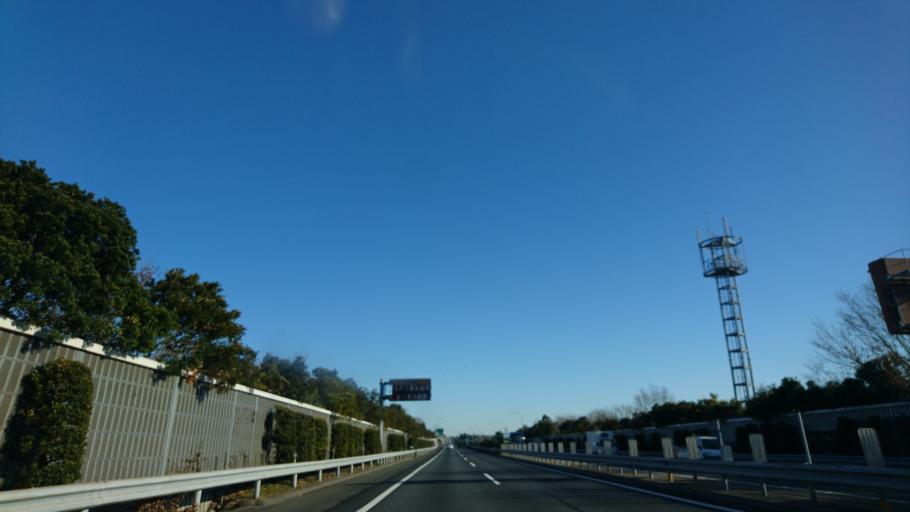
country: JP
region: Chiba
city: Ichihara
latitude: 35.4923
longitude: 140.0890
